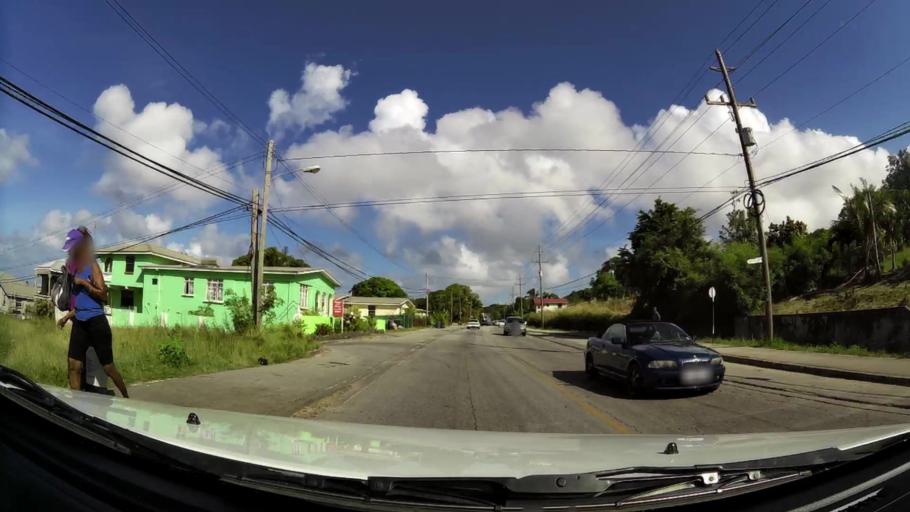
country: BB
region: Saint James
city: Holetown
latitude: 13.2207
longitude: -59.6216
